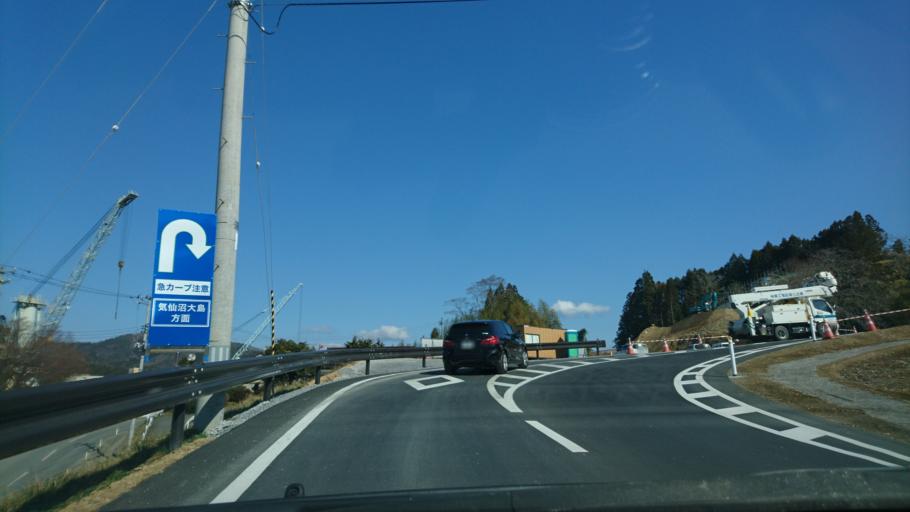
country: JP
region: Iwate
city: Ofunato
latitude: 38.9071
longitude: 141.5880
